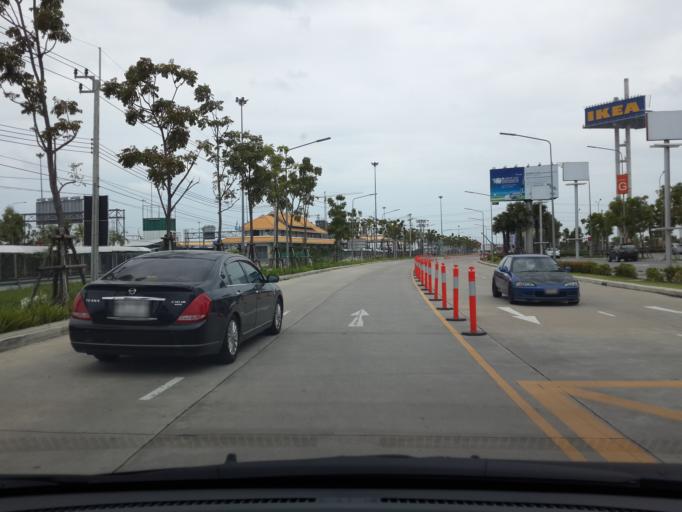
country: TH
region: Bangkok
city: Bang Na
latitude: 13.6458
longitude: 100.6825
